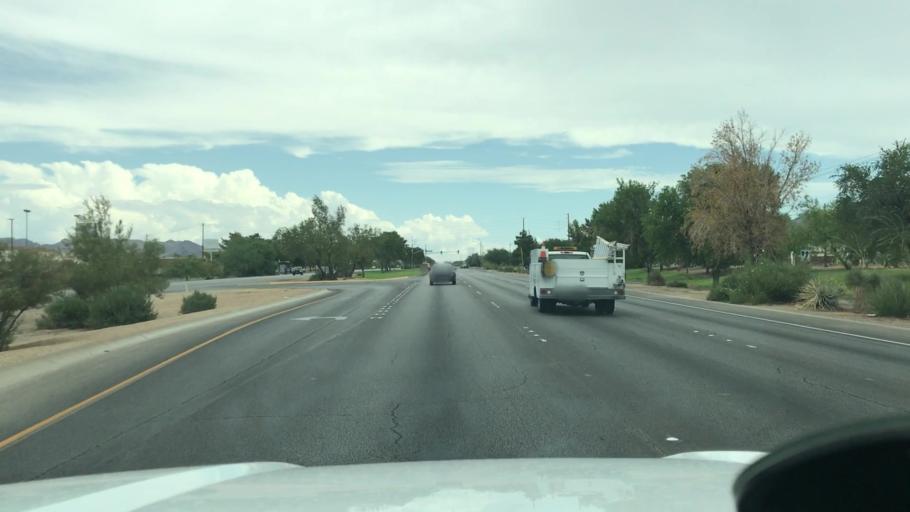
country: US
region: Nevada
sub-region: Clark County
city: Henderson
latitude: 36.0320
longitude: -114.9737
